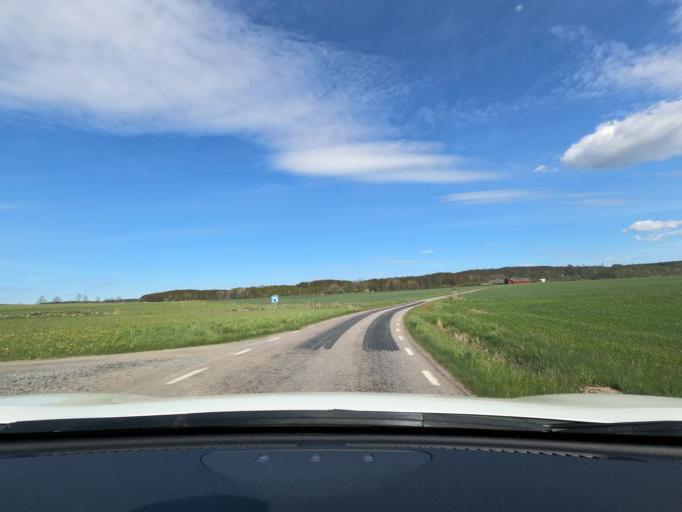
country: SE
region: Vaestra Goetaland
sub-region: Marks Kommun
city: Horred
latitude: 57.4564
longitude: 12.4944
